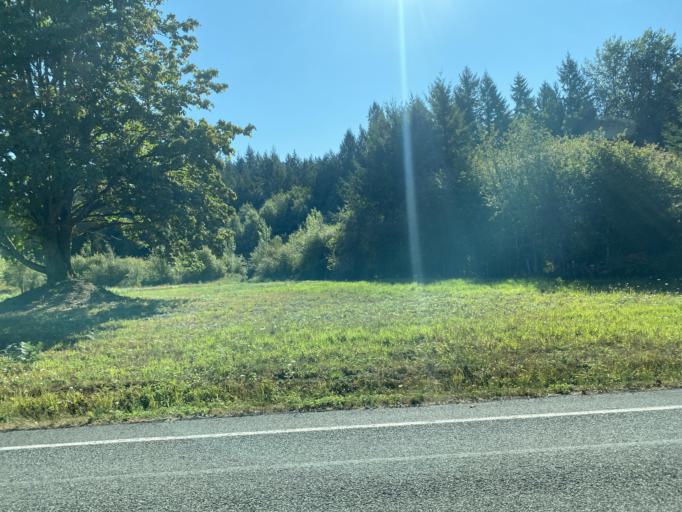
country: US
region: Washington
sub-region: Thurston County
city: Tanglewilde-Thompson Place
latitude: 46.9571
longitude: -122.7673
